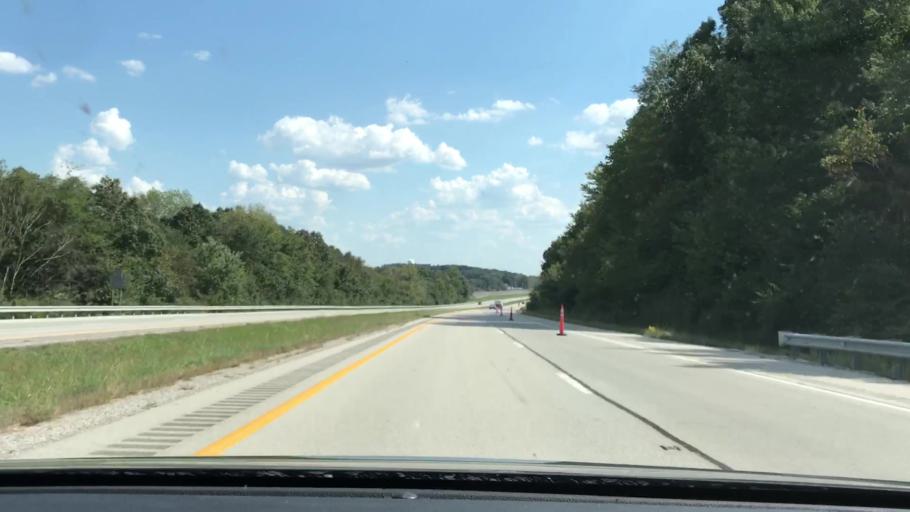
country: US
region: Kentucky
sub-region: Butler County
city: Morgantown
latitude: 37.2223
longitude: -86.7170
